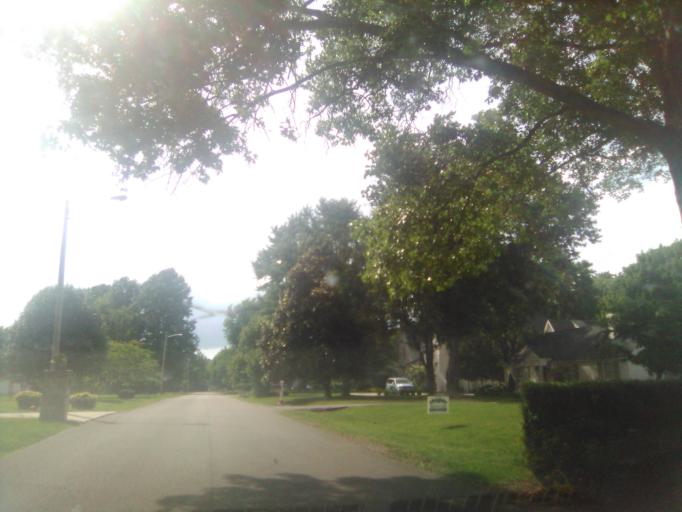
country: US
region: Tennessee
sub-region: Davidson County
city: Belle Meade
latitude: 36.0948
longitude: -86.8711
